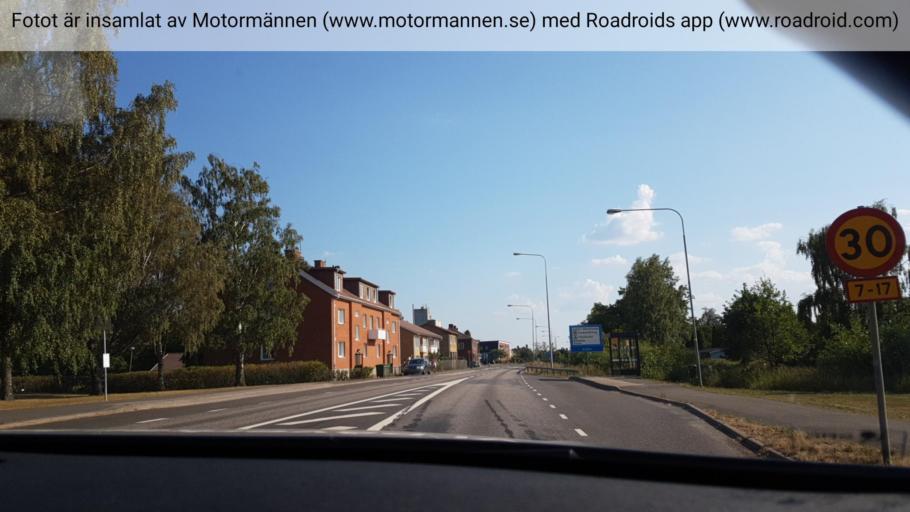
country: SE
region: Vaestra Goetaland
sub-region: Skovde Kommun
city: Stopen
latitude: 58.5731
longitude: 14.0047
